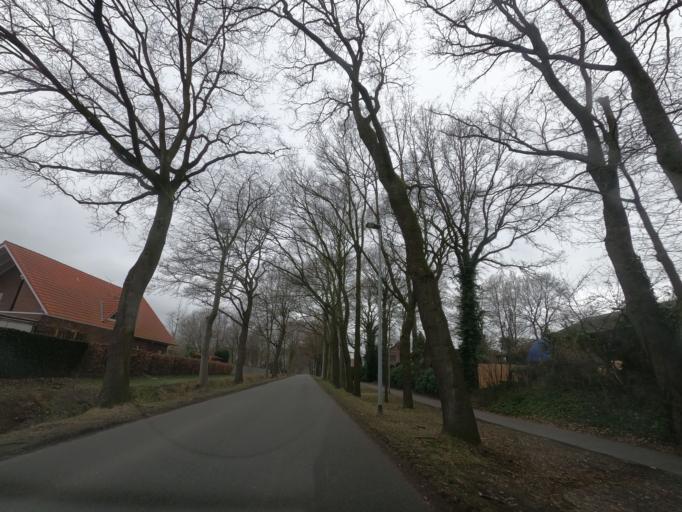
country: DE
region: Lower Saxony
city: Cloppenburg
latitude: 52.8362
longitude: 8.0056
